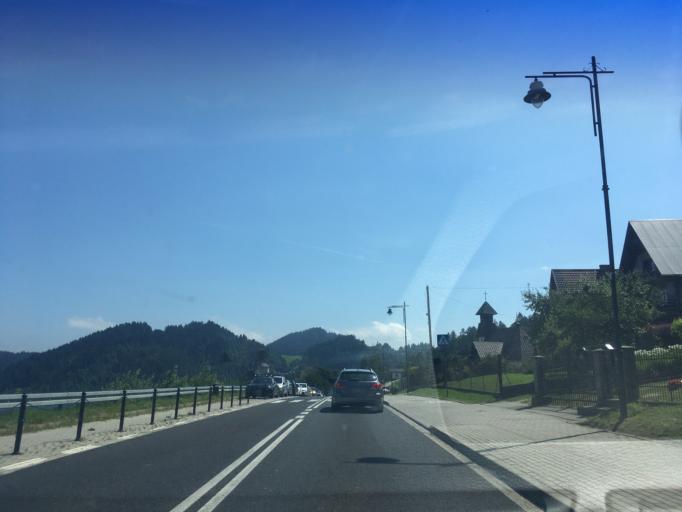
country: PL
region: Lesser Poland Voivodeship
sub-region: Powiat nowotarski
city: Niedzica
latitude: 49.4242
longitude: 20.3075
